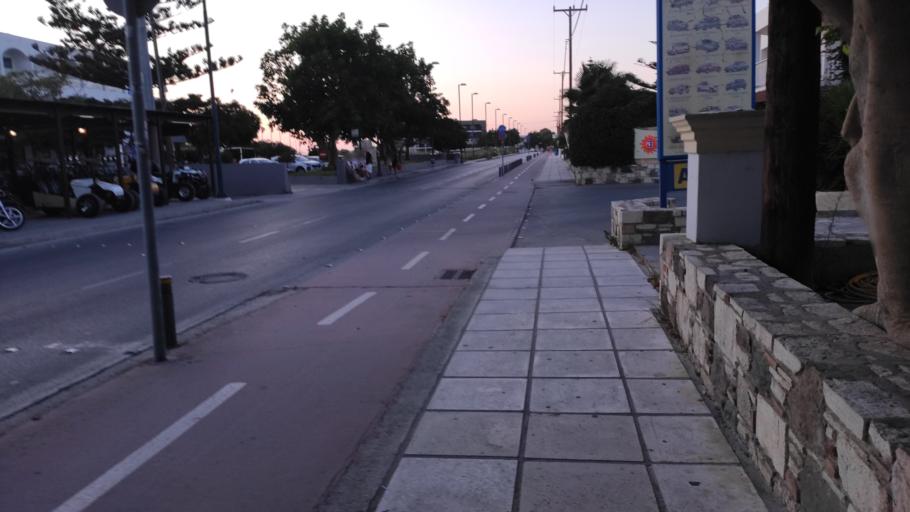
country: GR
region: South Aegean
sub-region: Nomos Dodekanisou
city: Kos
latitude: 36.9120
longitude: 27.2787
